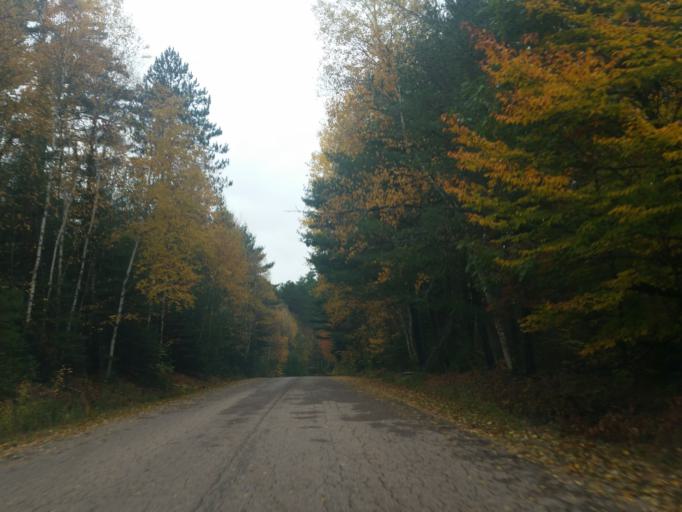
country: CA
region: Ontario
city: Deep River
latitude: 45.9922
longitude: -77.4040
